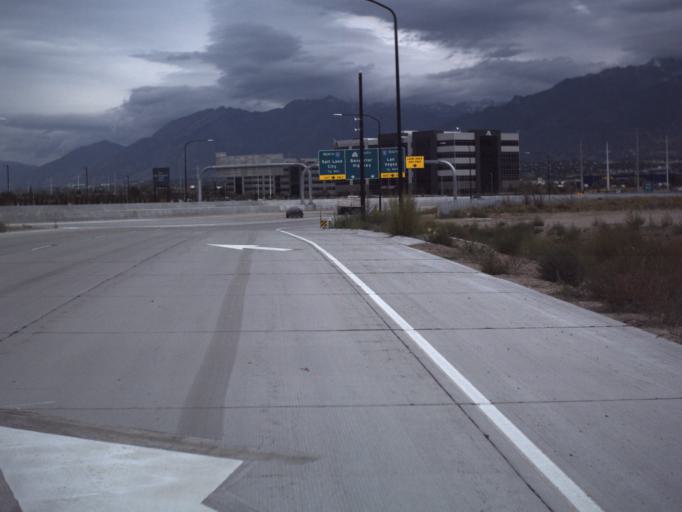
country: US
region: Utah
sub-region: Salt Lake County
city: Bluffdale
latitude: 40.5015
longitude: -111.9056
